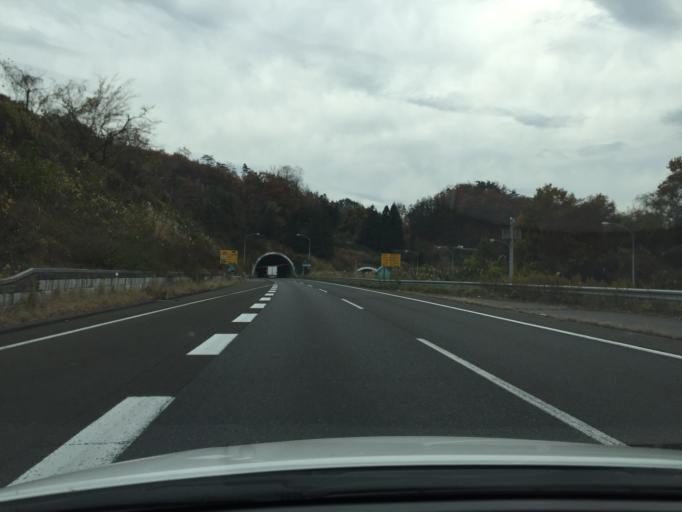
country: JP
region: Fukushima
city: Fukushima-shi
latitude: 37.6876
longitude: 140.4440
